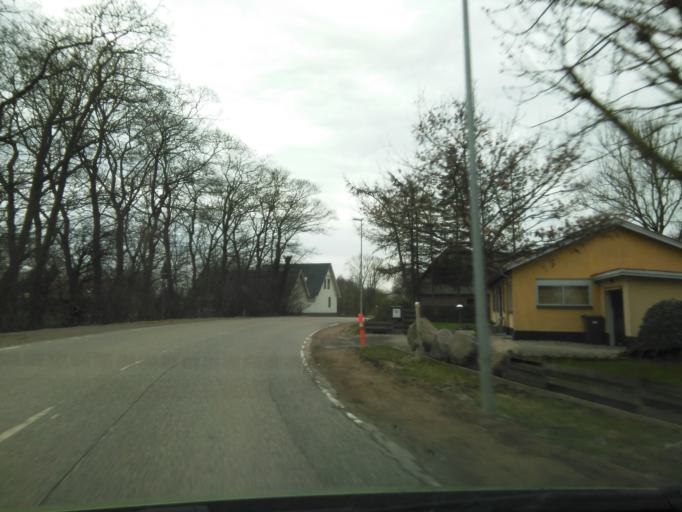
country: DK
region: Central Jutland
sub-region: Randers Kommune
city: Spentrup
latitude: 56.5568
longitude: 10.0015
